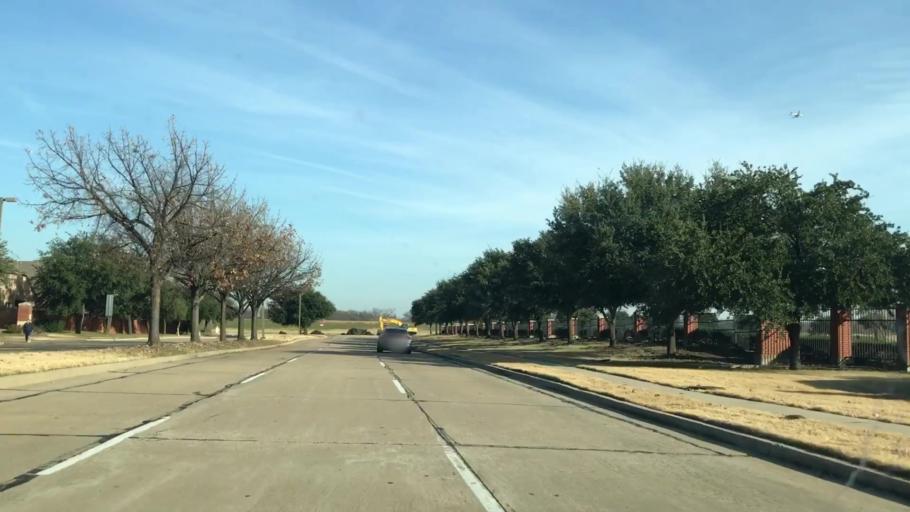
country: US
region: Texas
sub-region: Dallas County
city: Farmers Branch
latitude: 32.9216
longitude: -96.9462
